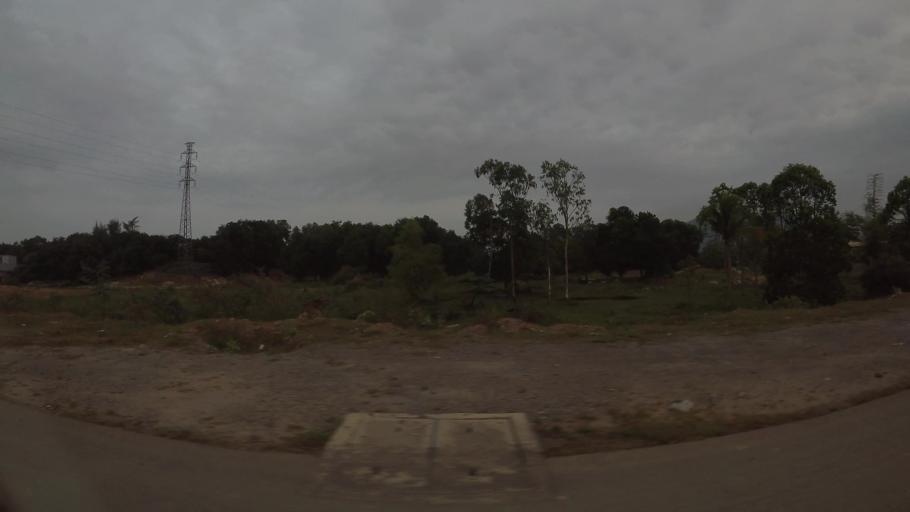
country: VN
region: Da Nang
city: Lien Chieu
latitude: 16.0936
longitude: 108.1104
